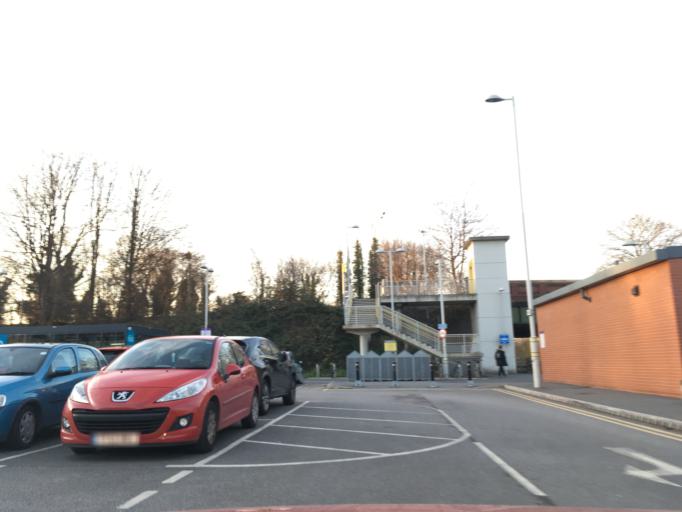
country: GB
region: England
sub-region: Manchester
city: Didsbury
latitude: 53.4120
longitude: -2.2176
